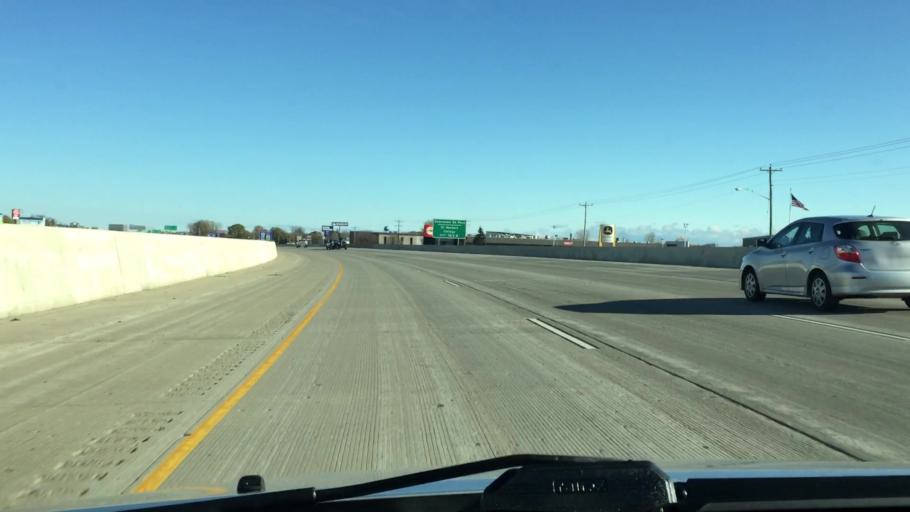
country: US
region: Wisconsin
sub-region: Brown County
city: De Pere
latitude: 44.4383
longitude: -88.1000
